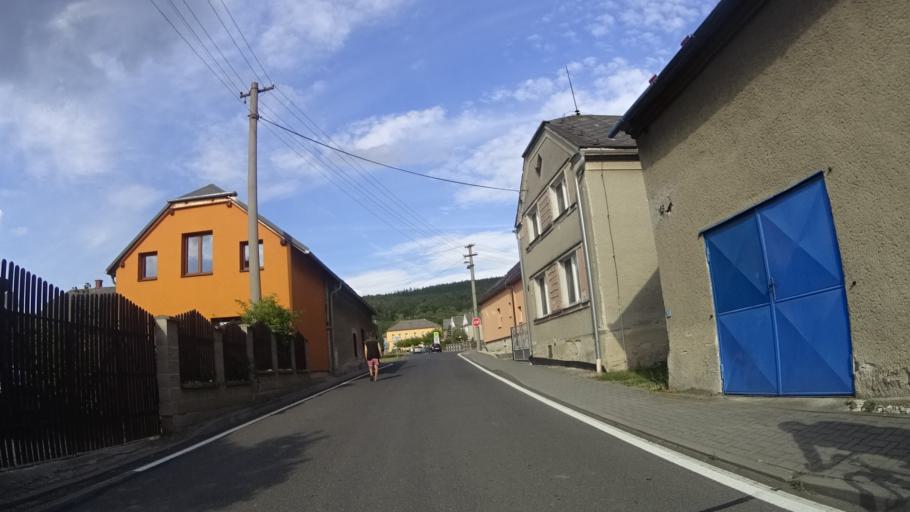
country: CZ
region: Olomoucky
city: Dubicko
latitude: 49.8446
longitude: 16.9508
